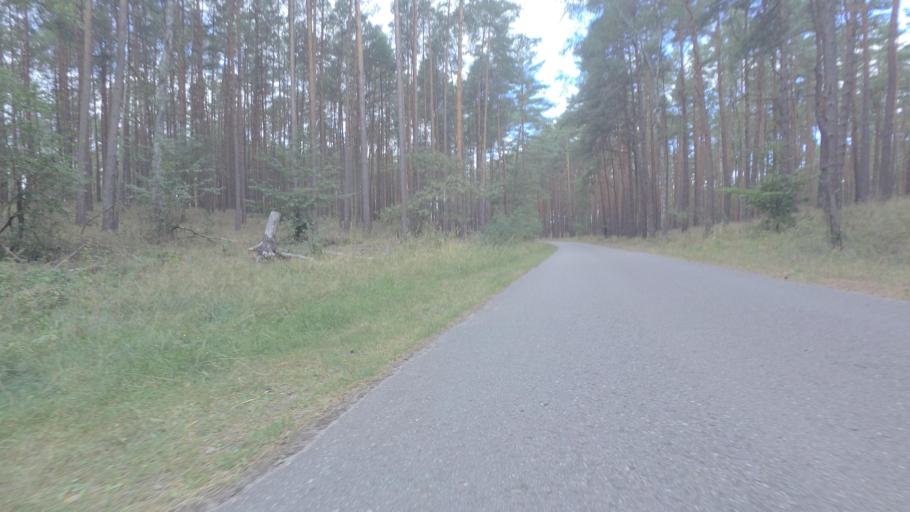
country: DE
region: Brandenburg
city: Wittstock
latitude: 53.0796
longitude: 12.4813
